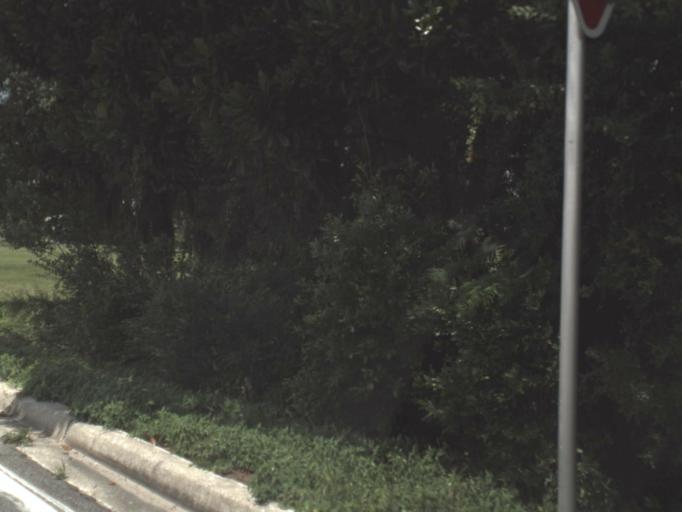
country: US
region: Florida
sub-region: Hamilton County
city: Jasper
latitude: 30.4893
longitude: -82.9302
